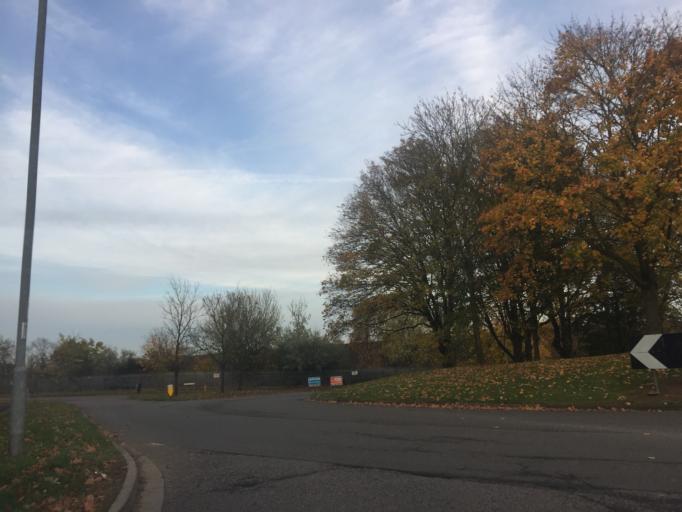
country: GB
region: England
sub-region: Northamptonshire
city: Northampton
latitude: 52.2783
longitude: -0.8392
